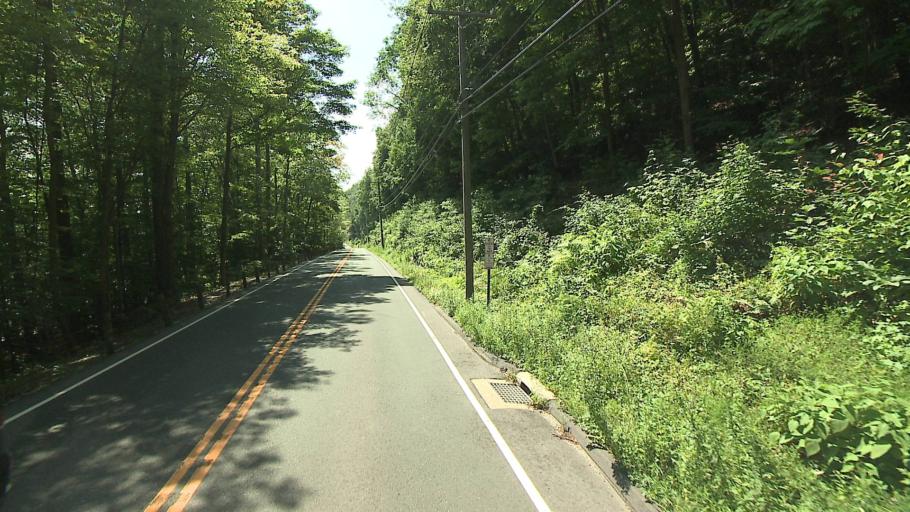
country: US
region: New York
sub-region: Putnam County
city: Putnam Lake
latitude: 41.4974
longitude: -73.4696
